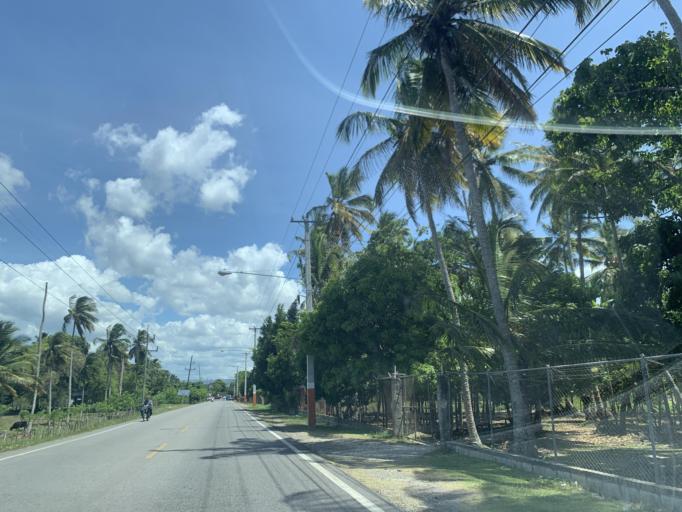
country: DO
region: Puerto Plata
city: Cabarete
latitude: 19.7130
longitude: -70.3853
